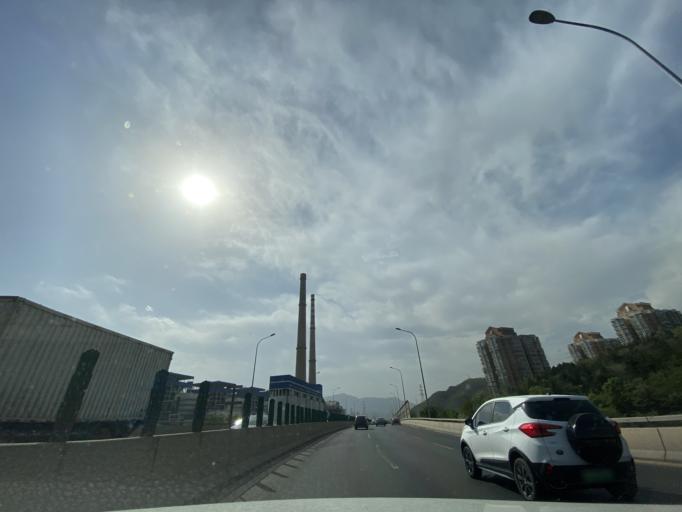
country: CN
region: Beijing
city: Guangning
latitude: 39.9230
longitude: 116.1425
